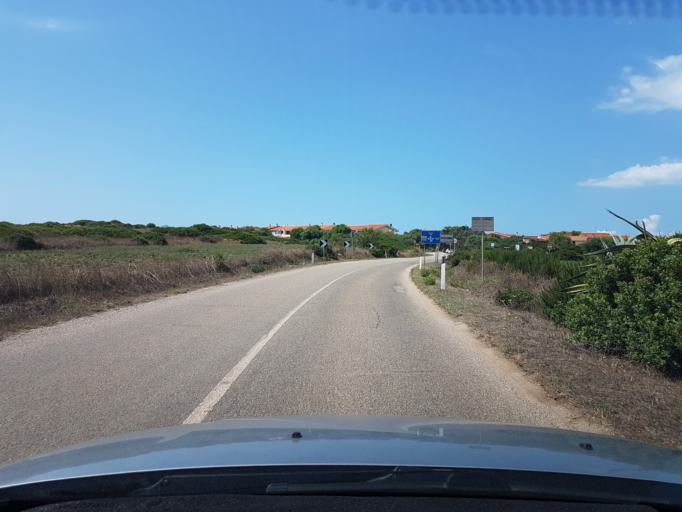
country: IT
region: Sardinia
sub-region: Provincia di Oristano
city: Riola Sardo
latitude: 40.0380
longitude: 8.4182
